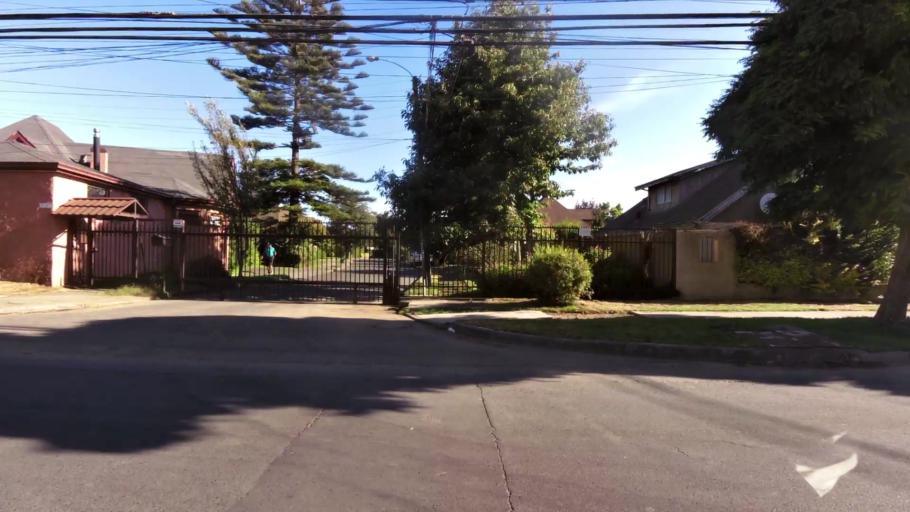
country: CL
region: Biobio
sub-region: Provincia de Concepcion
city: Concepcion
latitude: -36.8346
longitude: -73.1061
